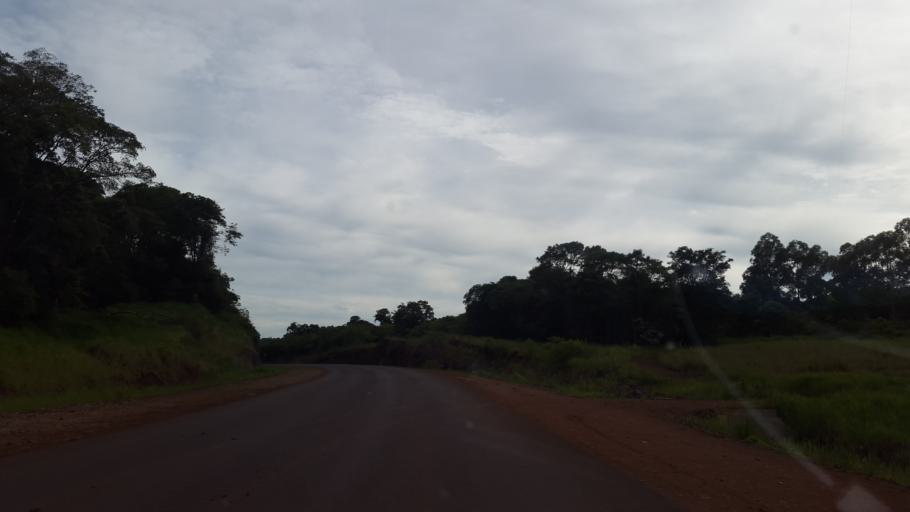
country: AR
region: Misiones
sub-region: Departamento de San Pedro
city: San Pedro
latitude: -26.4747
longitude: -53.8778
